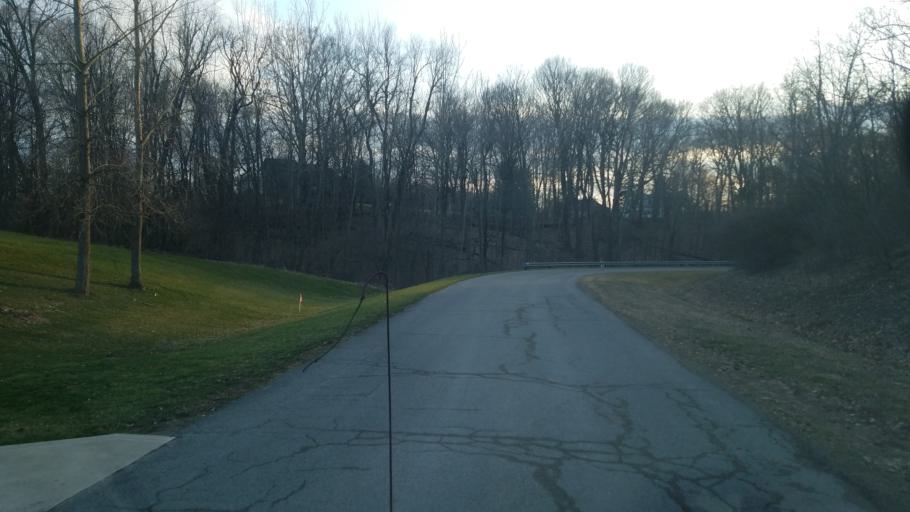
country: US
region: Ohio
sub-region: Logan County
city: West Liberty
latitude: 40.2352
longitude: -83.7173
